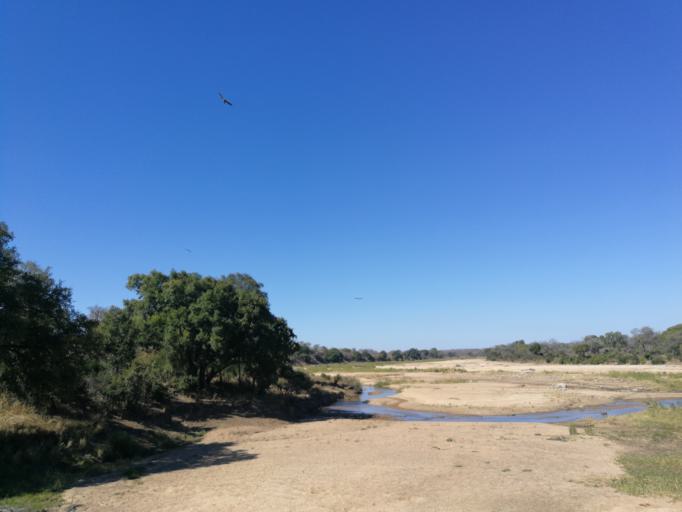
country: ZA
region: Limpopo
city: Thulamahashi
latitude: -24.9424
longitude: 31.6775
